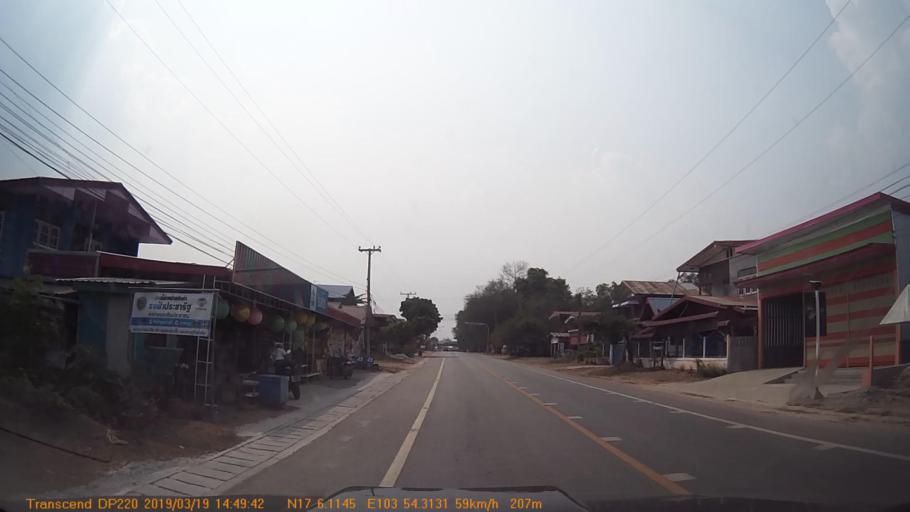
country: TH
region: Sakon Nakhon
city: Kut Bak
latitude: 17.1020
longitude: 103.9050
